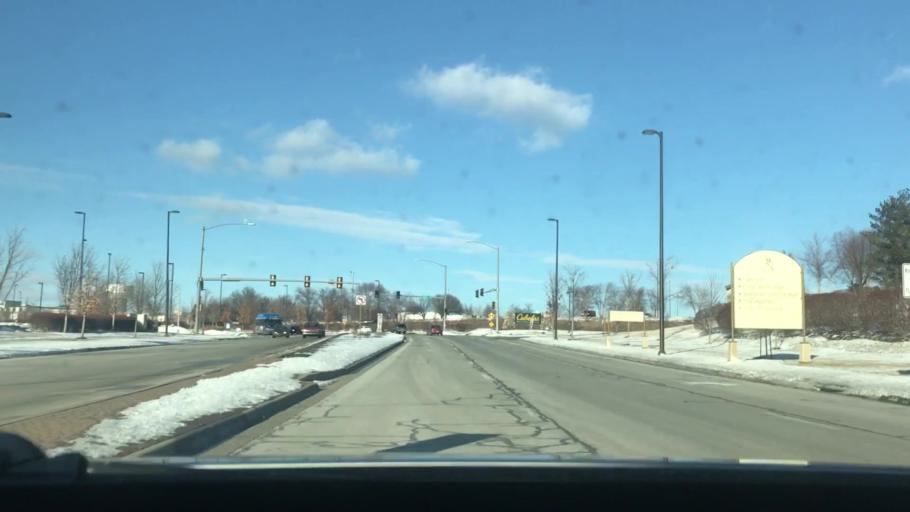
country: US
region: Kansas
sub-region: Wyandotte County
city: Edwardsville
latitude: 39.1176
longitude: -94.8190
